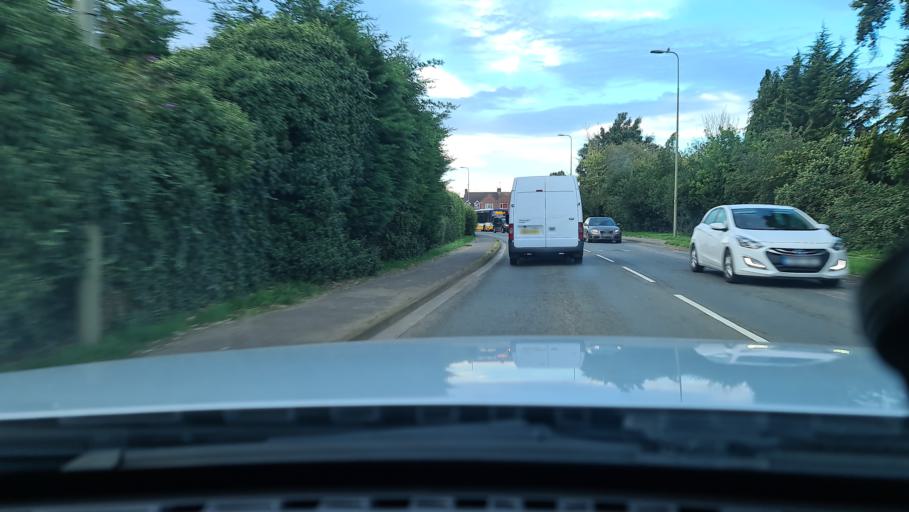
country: GB
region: England
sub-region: Oxfordshire
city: Banbury
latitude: 52.0693
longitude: -1.3610
